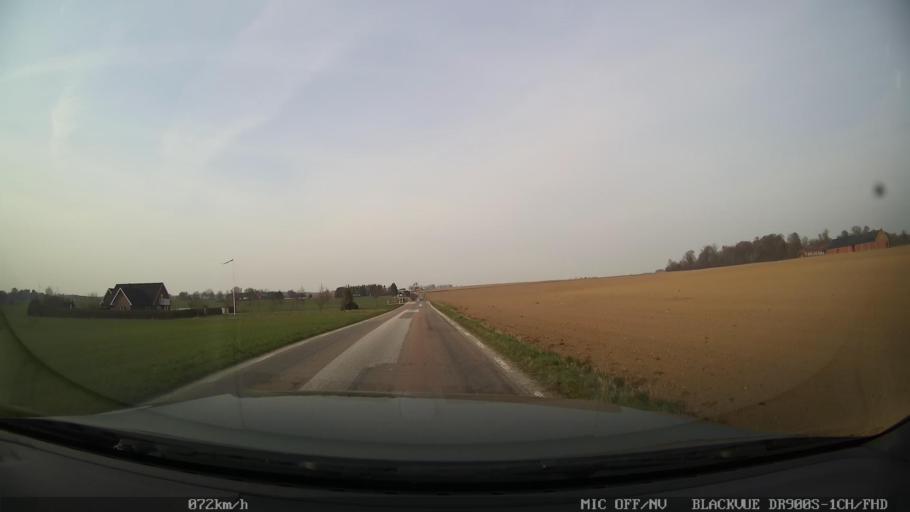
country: SE
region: Skane
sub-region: Ystads Kommun
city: Ystad
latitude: 55.4504
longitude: 13.8313
